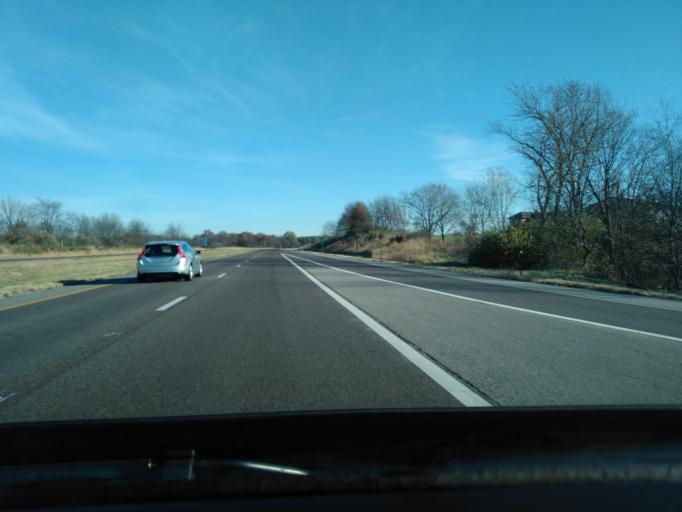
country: US
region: Illinois
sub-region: Madison County
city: Saint Jacob
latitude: 38.7786
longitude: -89.7405
